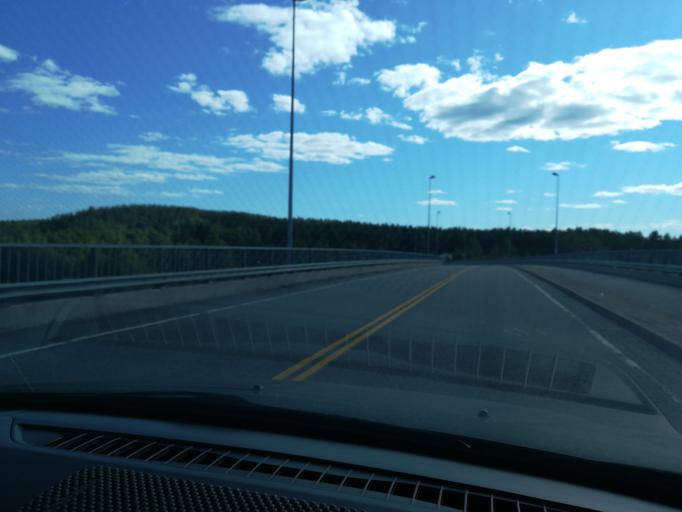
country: FI
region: Southern Savonia
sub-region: Mikkeli
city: Puumala
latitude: 61.5186
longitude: 28.1755
